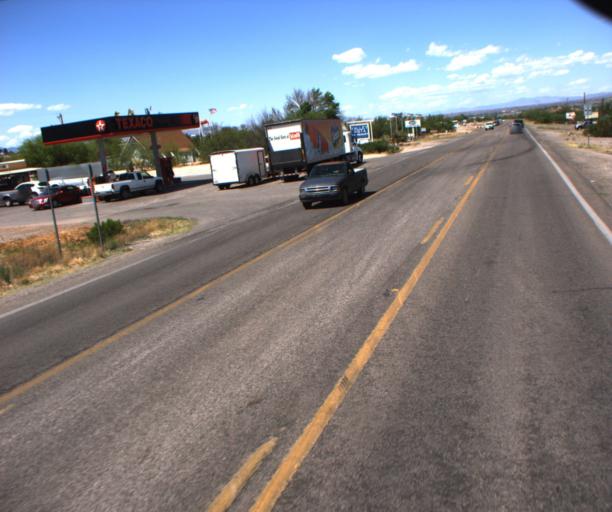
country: US
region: Arizona
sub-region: Cochise County
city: Benson
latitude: 31.9494
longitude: -110.2860
